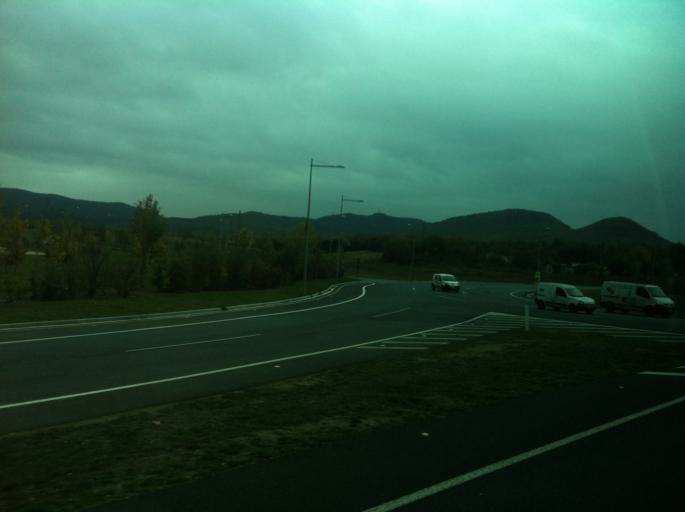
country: ES
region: Basque Country
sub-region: Provincia de Alava
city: Gasteiz / Vitoria
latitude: 42.8343
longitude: -2.7090
